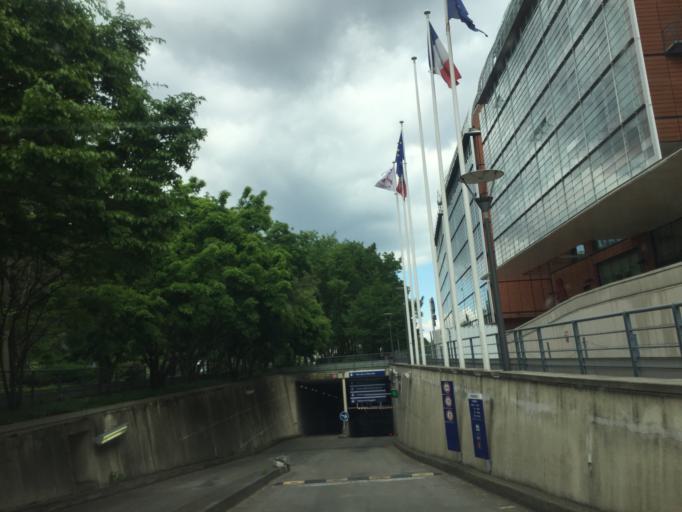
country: FR
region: Rhone-Alpes
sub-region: Departement du Rhone
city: Caluire-et-Cuire
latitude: 45.7849
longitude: 4.8525
